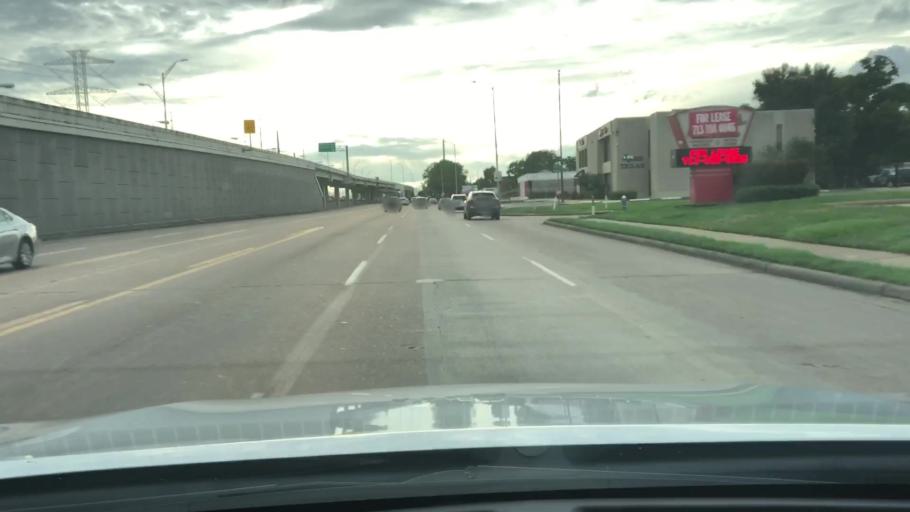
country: US
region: Texas
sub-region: Harris County
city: Piney Point Village
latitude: 29.7225
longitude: -95.5089
